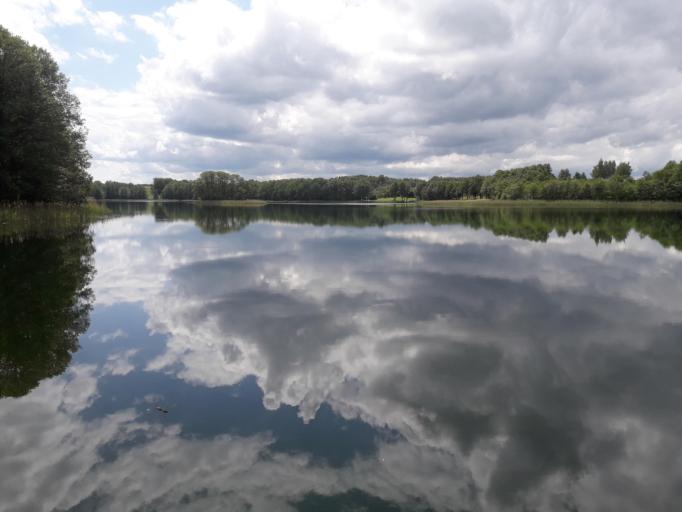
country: LT
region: Alytaus apskritis
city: Druskininkai
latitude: 54.1089
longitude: 24.0203
